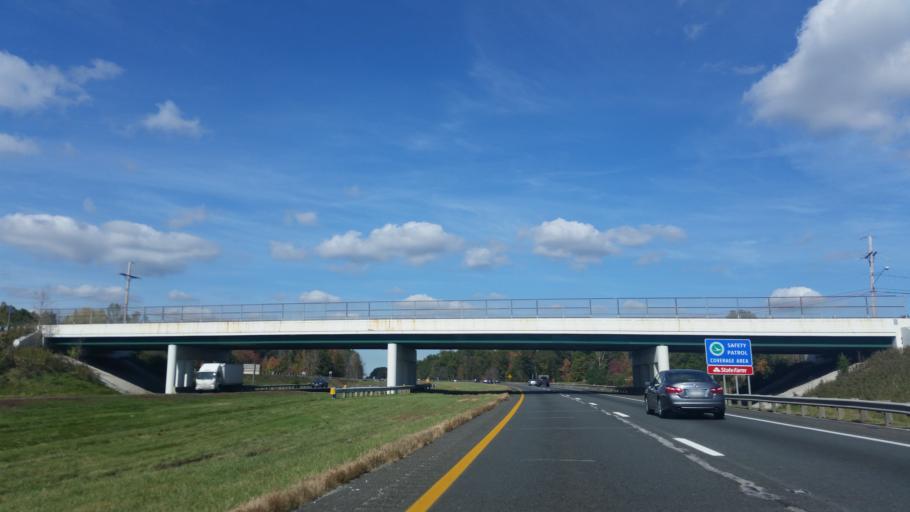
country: US
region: Ohio
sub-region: Cuyahoga County
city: Brecksville
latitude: 41.2886
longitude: -81.6364
